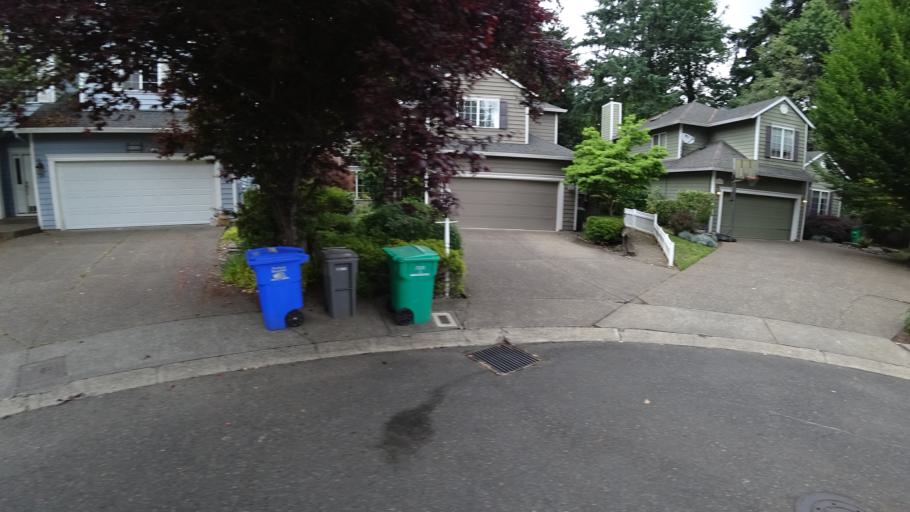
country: US
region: Oregon
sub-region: Washington County
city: Garden Home-Whitford
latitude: 45.4563
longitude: -122.7080
